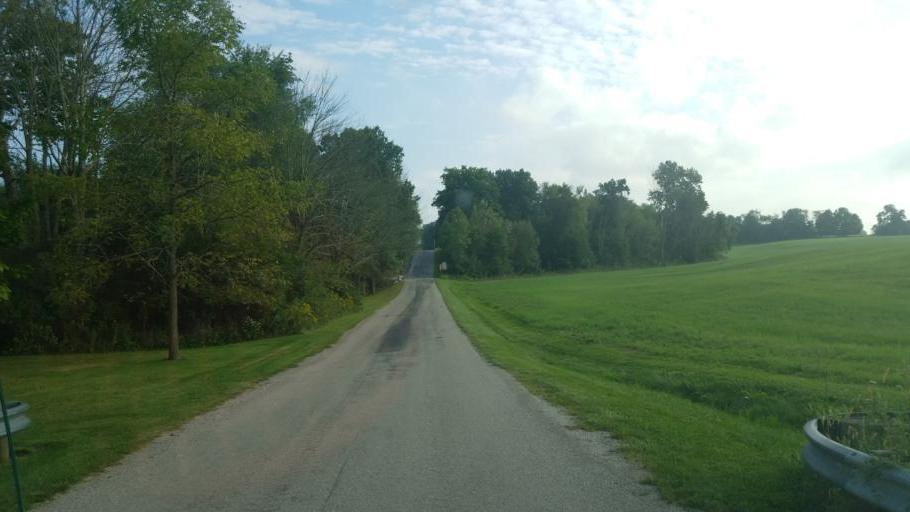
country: US
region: Ohio
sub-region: Wayne County
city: Wooster
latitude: 40.8257
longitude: -82.0436
